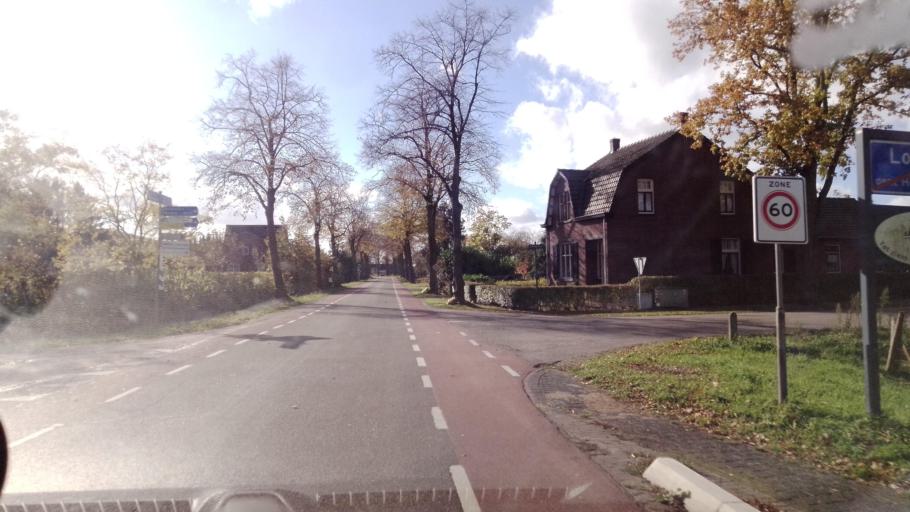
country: NL
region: Limburg
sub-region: Gemeente Venlo
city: Arcen
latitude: 51.4551
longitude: 6.1567
